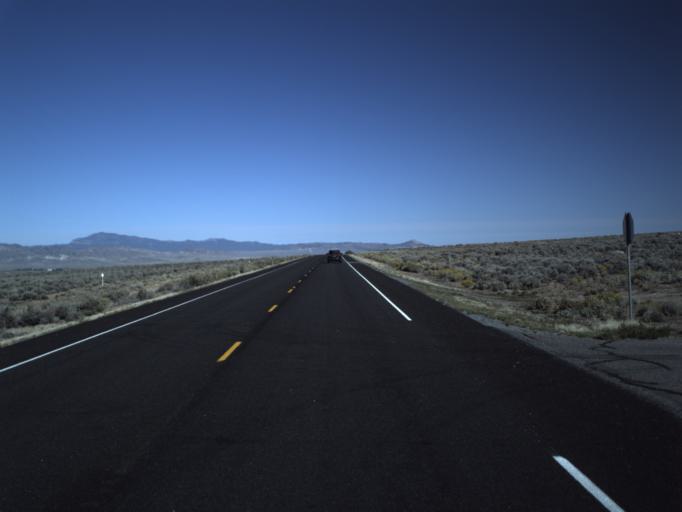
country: US
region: Utah
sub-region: Beaver County
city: Milford
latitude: 38.2472
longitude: -112.9435
